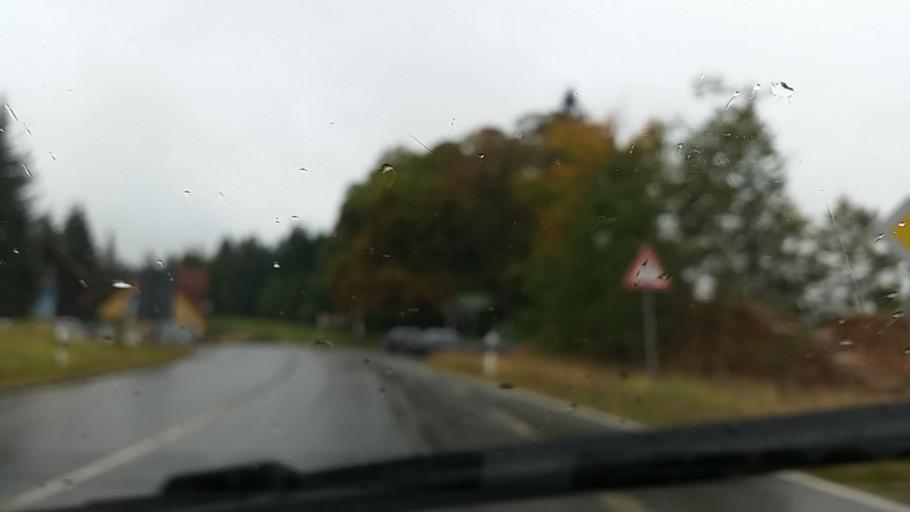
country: DE
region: Lower Saxony
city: Altenau
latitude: 51.7767
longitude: 10.4228
